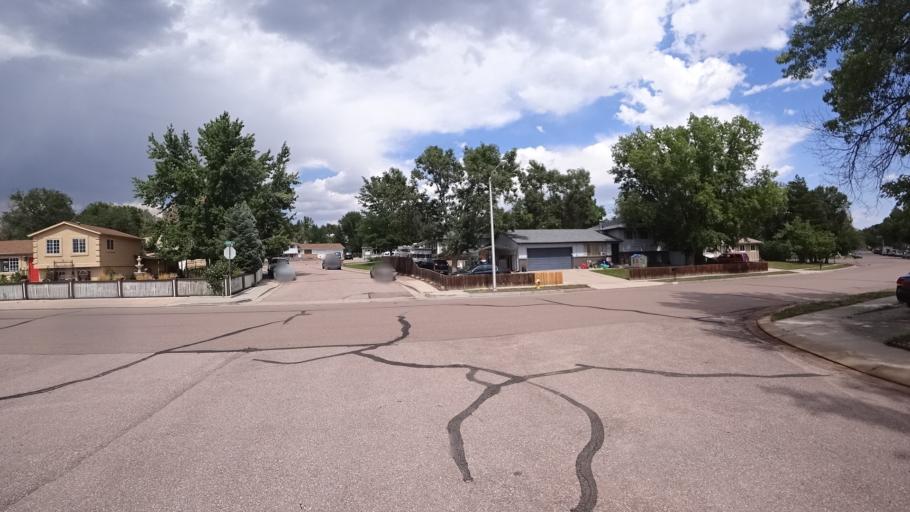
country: US
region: Colorado
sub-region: El Paso County
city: Cimarron Hills
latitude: 38.8295
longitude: -104.7459
